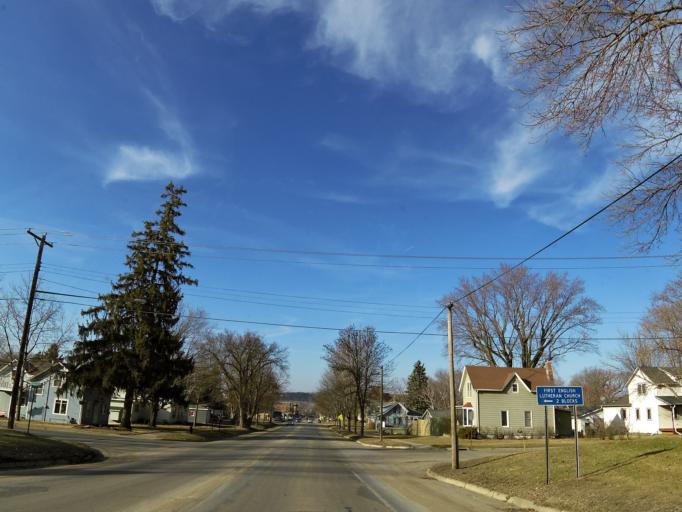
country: US
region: Minnesota
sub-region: Goodhue County
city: Cannon Falls
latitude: 44.5034
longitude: -92.9057
